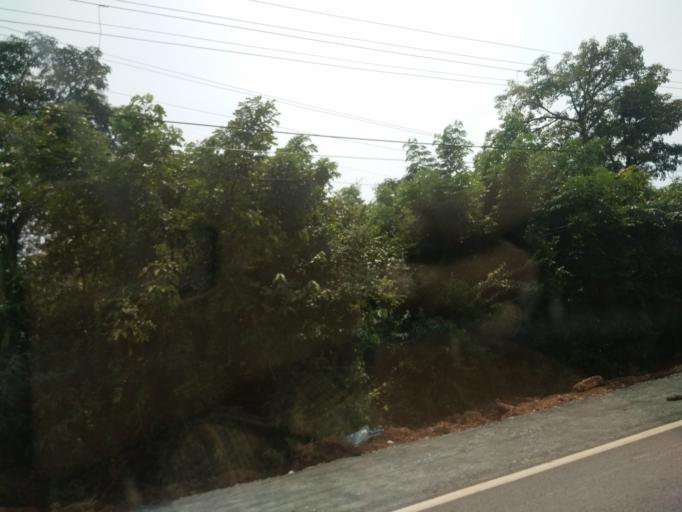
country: IN
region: Goa
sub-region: North Goa
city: Bambolim
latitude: 15.4666
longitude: 73.8623
